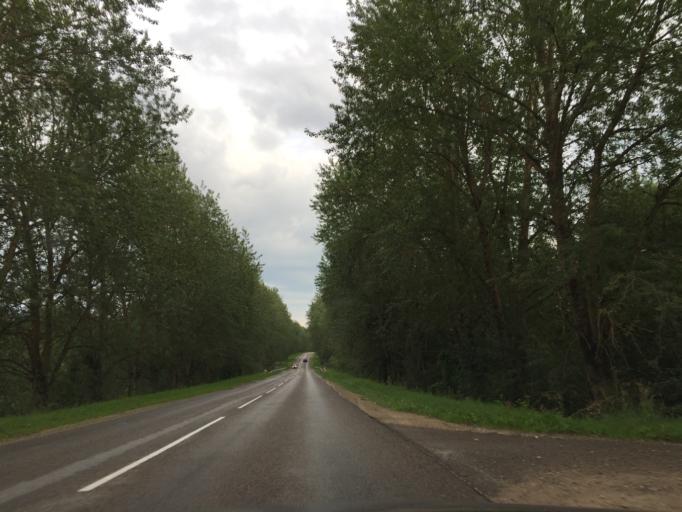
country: LV
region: Dobeles Rajons
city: Dobele
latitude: 56.5851
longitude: 23.2920
